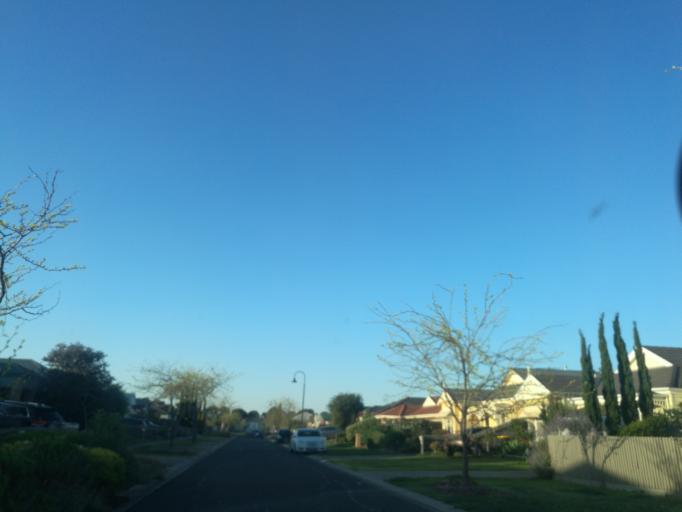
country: AU
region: Victoria
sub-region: Wyndham
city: Williams Landing
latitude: -37.8817
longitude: 144.7431
